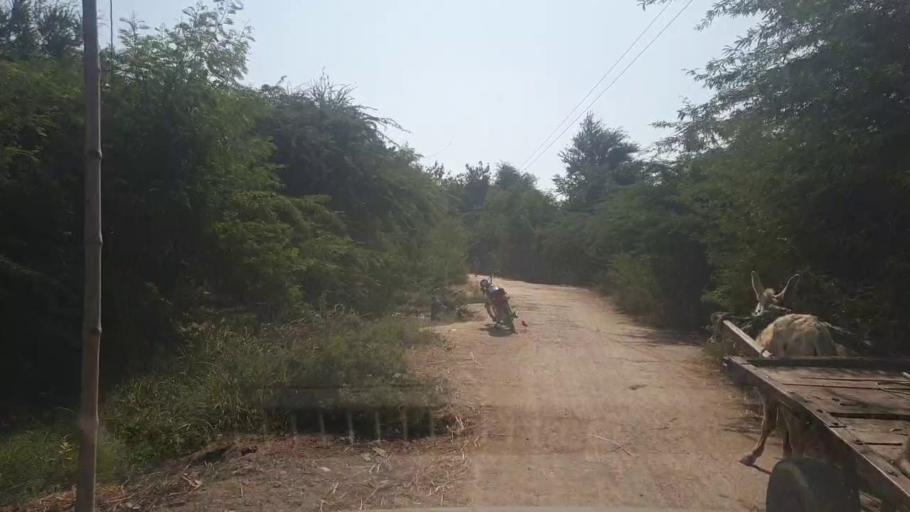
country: PK
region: Sindh
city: Badin
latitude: 24.6832
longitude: 68.8782
